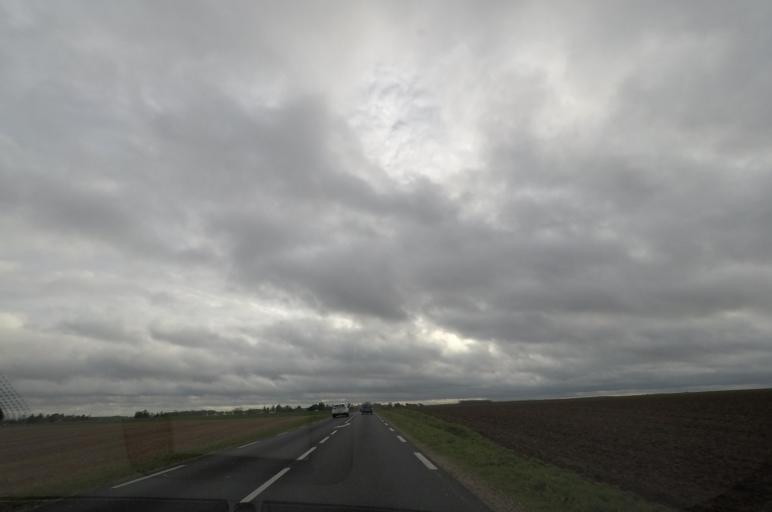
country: FR
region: Centre
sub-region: Departement du Loir-et-Cher
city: Herbault
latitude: 47.6954
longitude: 1.1853
